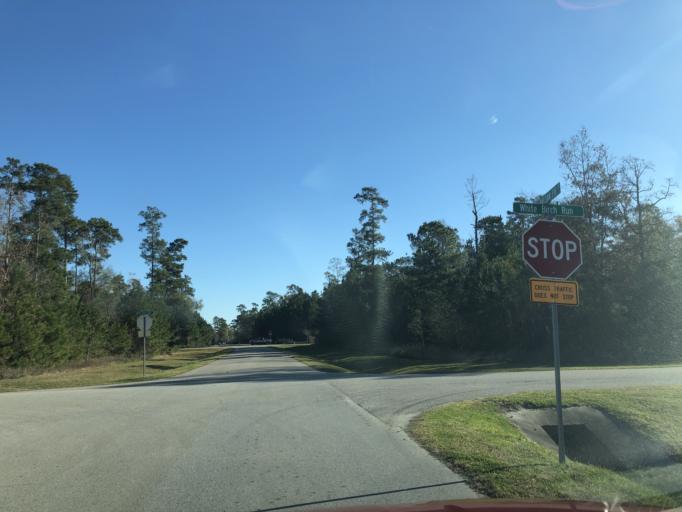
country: US
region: Texas
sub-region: Montgomery County
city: Porter Heights
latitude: 30.0824
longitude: -95.3341
